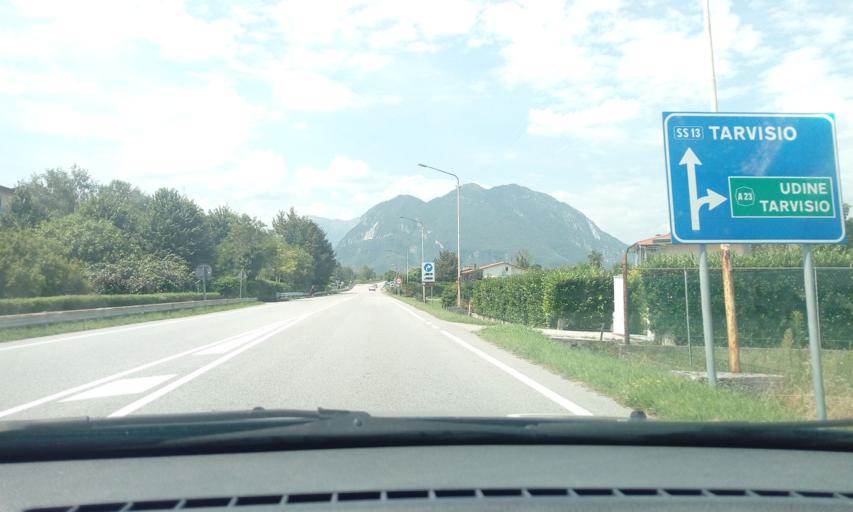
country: IT
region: Friuli Venezia Giulia
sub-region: Provincia di Udine
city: Gemona
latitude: 46.2553
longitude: 13.1126
